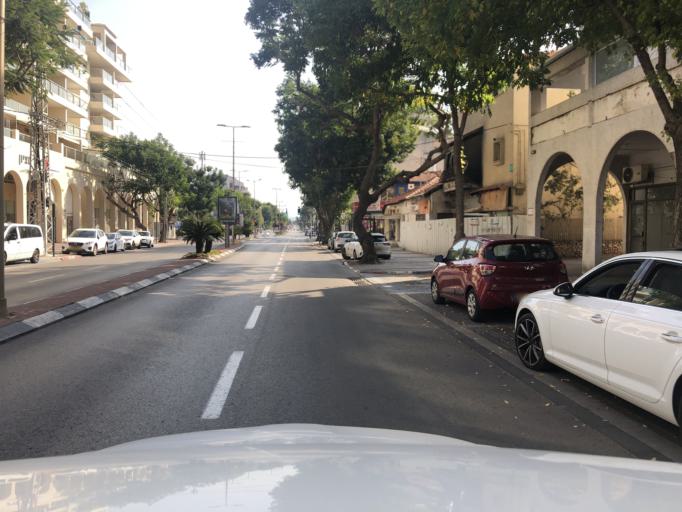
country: IL
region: Central District
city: Kfar Saba
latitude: 32.1743
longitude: 34.9126
